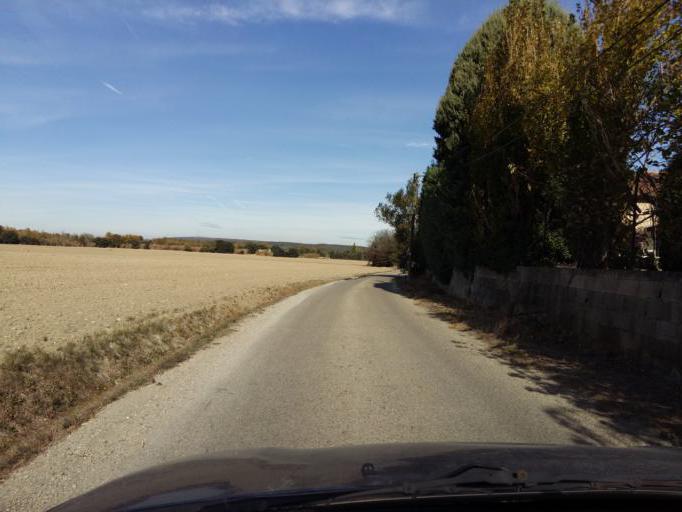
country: FR
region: Provence-Alpes-Cote d'Azur
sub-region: Departement du Vaucluse
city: Serignan-du-Comtat
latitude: 44.1668
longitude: 4.8355
